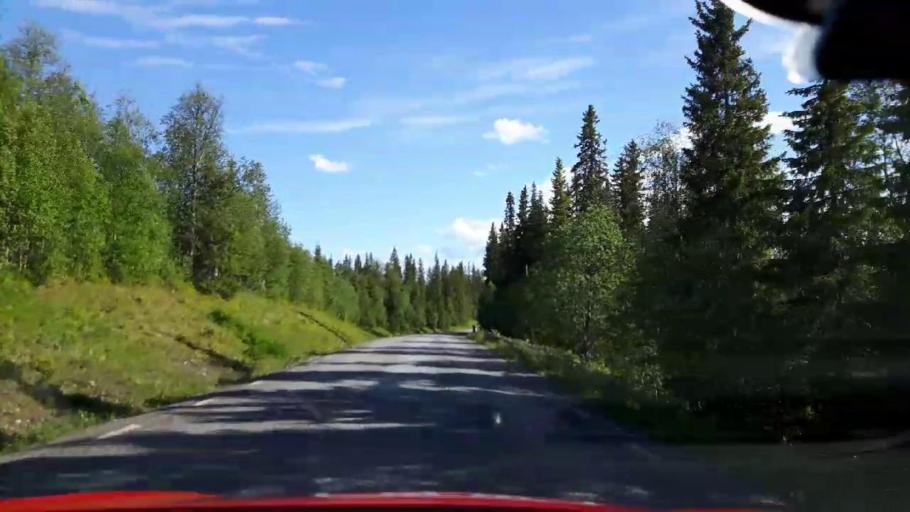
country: SE
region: Jaemtland
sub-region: Krokoms Kommun
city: Valla
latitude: 63.7148
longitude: 14.1354
